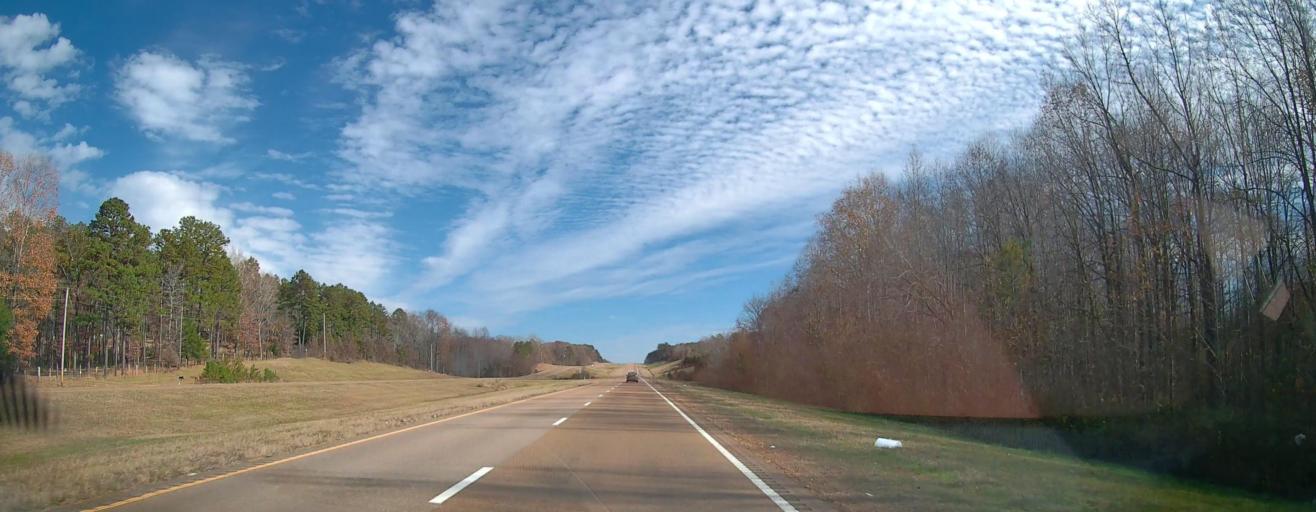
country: US
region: Mississippi
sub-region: Benton County
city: Ashland
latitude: 34.9523
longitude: -89.0551
